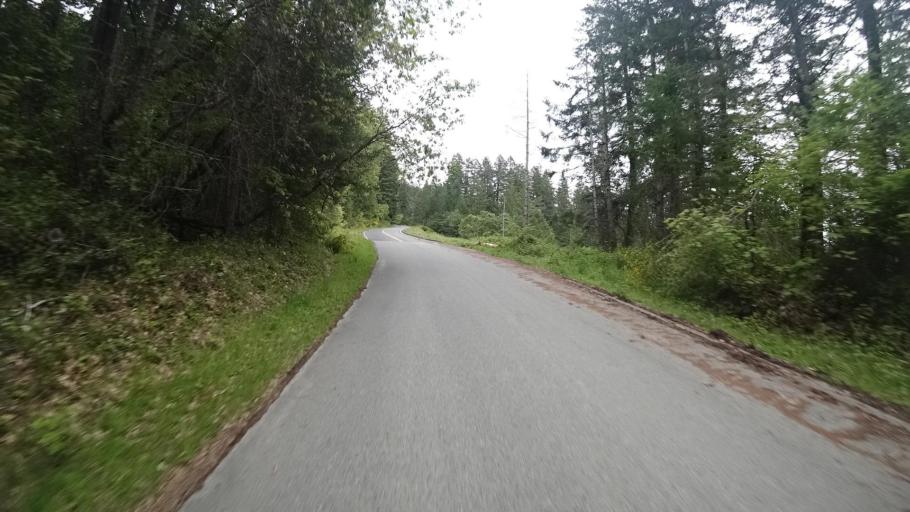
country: US
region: California
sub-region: Humboldt County
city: Willow Creek
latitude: 41.1236
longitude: -123.7474
